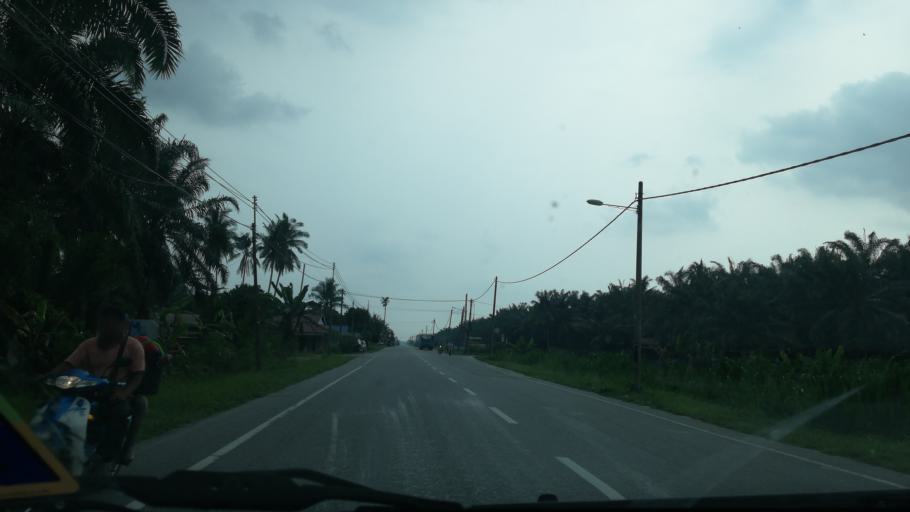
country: MY
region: Perak
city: Teluk Intan
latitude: 4.1136
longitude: 101.0695
